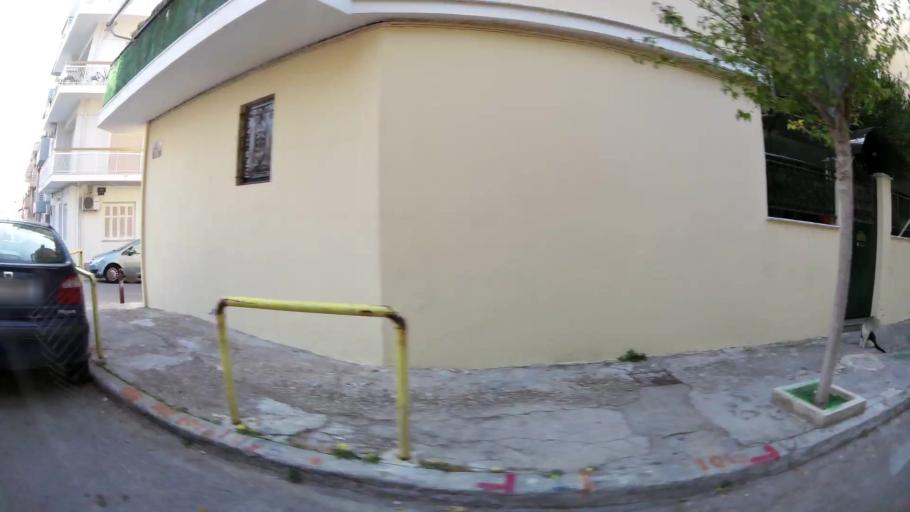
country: GR
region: Attica
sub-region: Nomarchia Athinas
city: Dhafni
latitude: 37.9485
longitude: 23.7277
